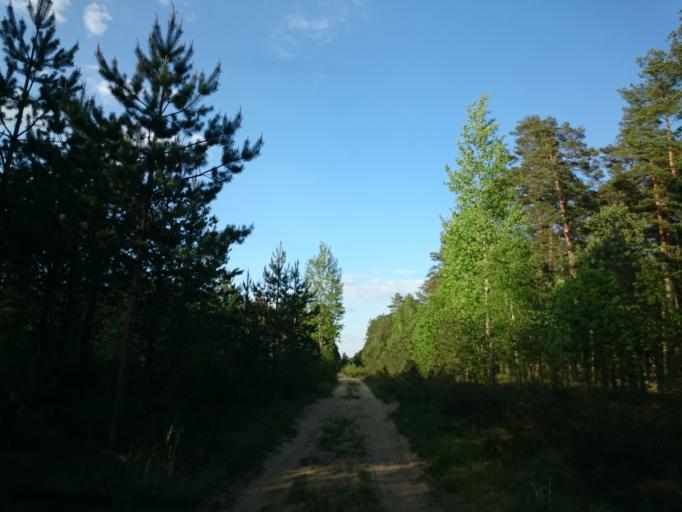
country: LV
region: Stopini
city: Ulbroka
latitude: 56.9520
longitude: 24.2911
